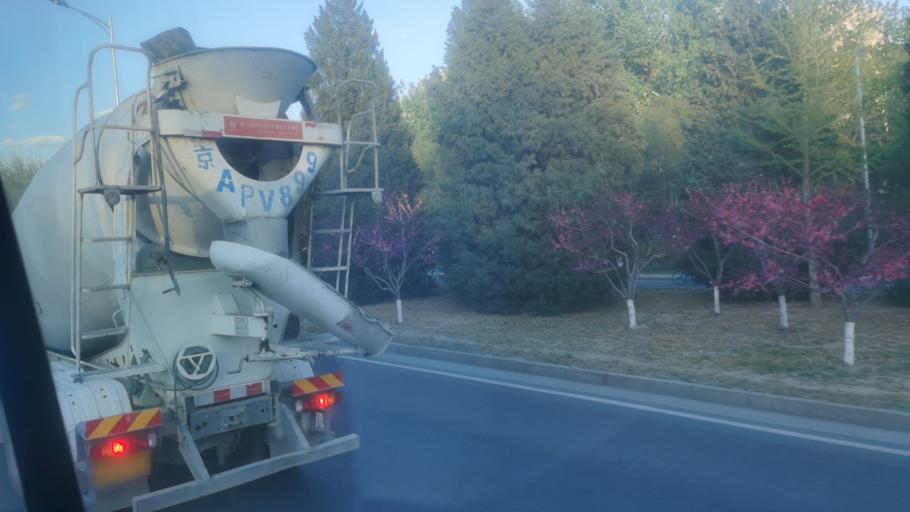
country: CN
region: Beijing
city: Xibeiwang
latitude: 40.0788
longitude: 116.2569
